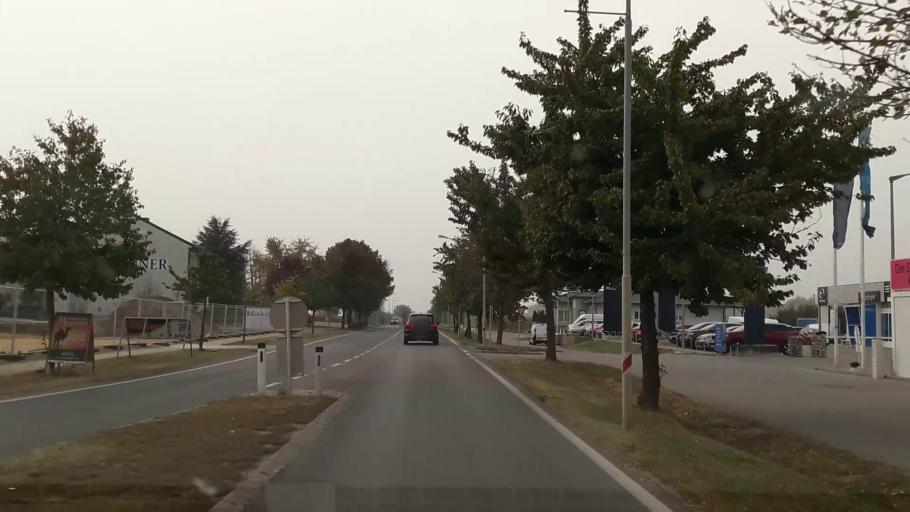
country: AT
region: Burgenland
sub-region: Politischer Bezirk Neusiedl am See
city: Gols
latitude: 47.9053
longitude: 16.8983
